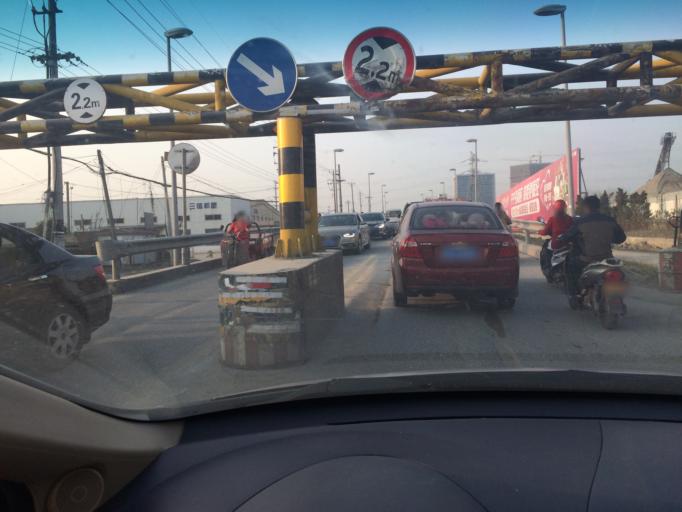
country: CN
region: Jiangsu Sheng
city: Guoxiang
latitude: 31.2593
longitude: 120.6700
